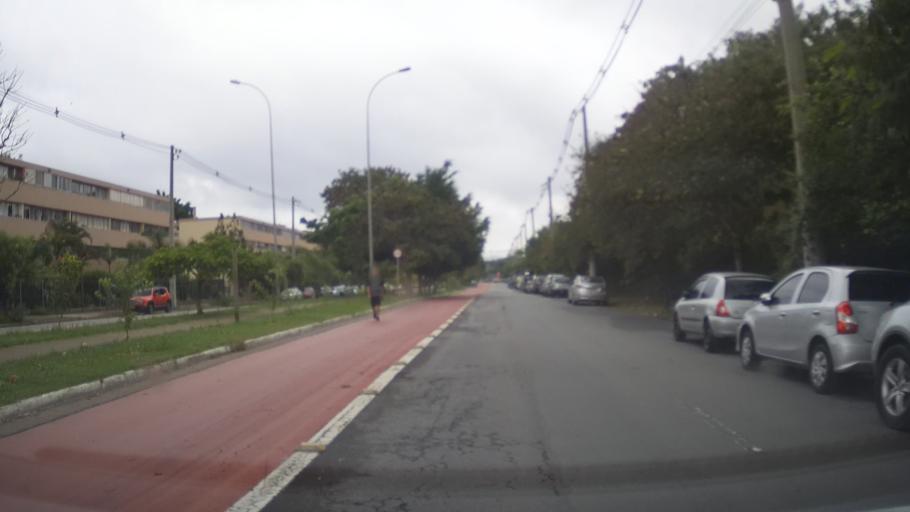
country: BR
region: Sao Paulo
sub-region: Guarulhos
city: Guarulhos
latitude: -23.4522
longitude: -46.4950
